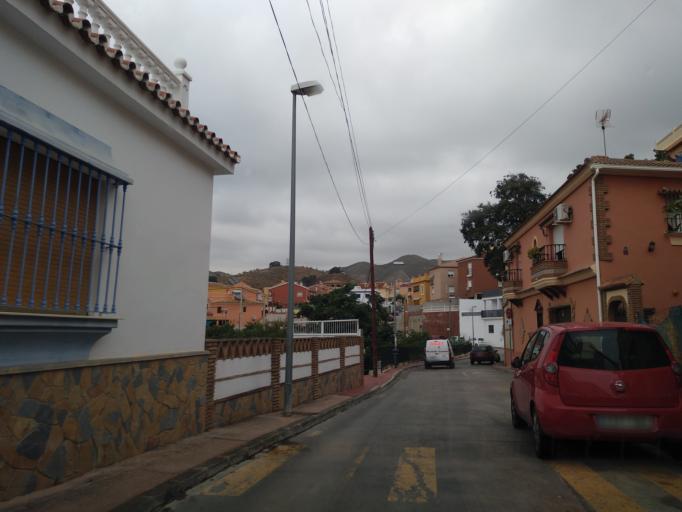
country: ES
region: Andalusia
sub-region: Provincia de Malaga
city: Malaga
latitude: 36.7444
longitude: -4.4779
